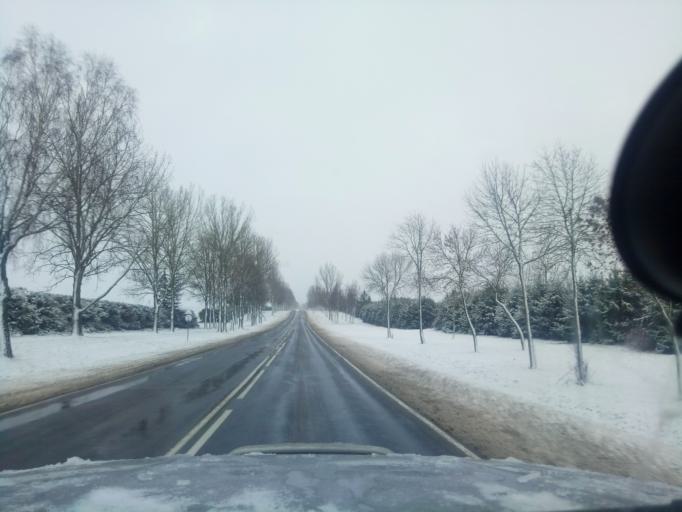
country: BY
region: Minsk
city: Haradzyeya
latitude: 53.3526
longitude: 26.5166
